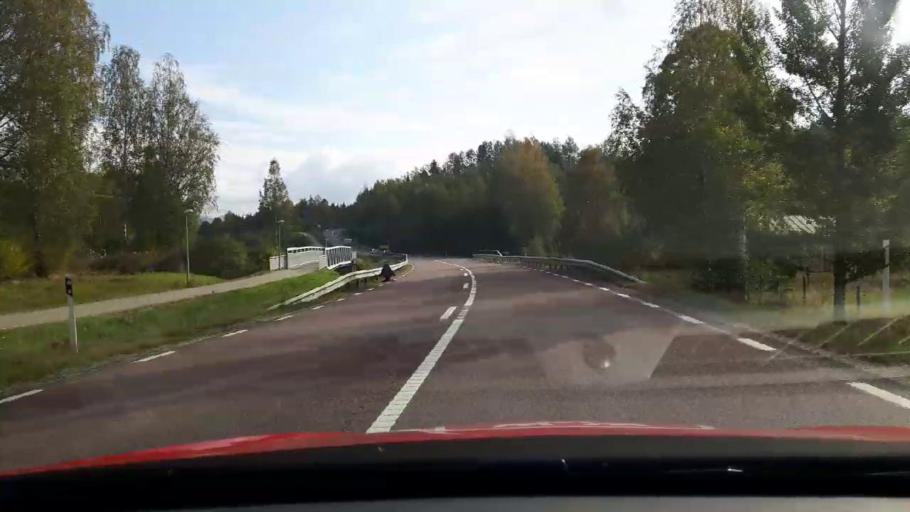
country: SE
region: Gaevleborg
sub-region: Bollnas Kommun
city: Kilafors
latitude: 61.2226
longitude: 16.5757
